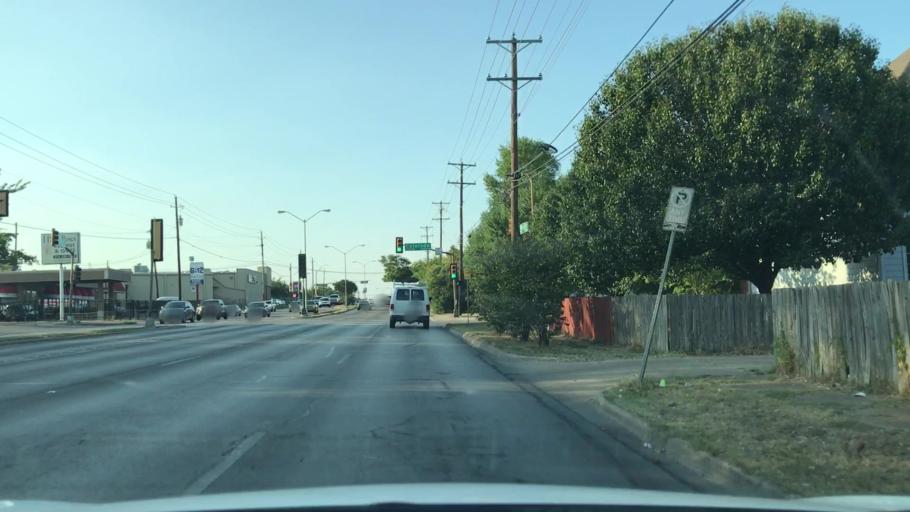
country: US
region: Texas
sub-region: Dallas County
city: Cockrell Hill
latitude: 32.7597
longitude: -96.8566
